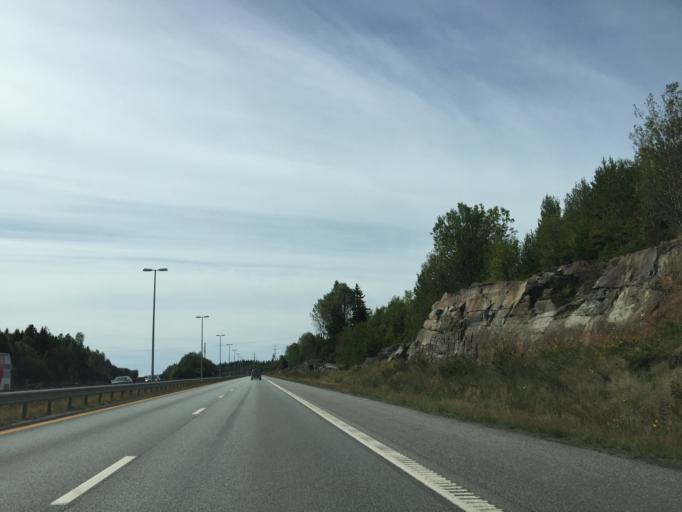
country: NO
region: Akershus
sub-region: Vestby
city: Vestby
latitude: 59.5761
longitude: 10.7272
